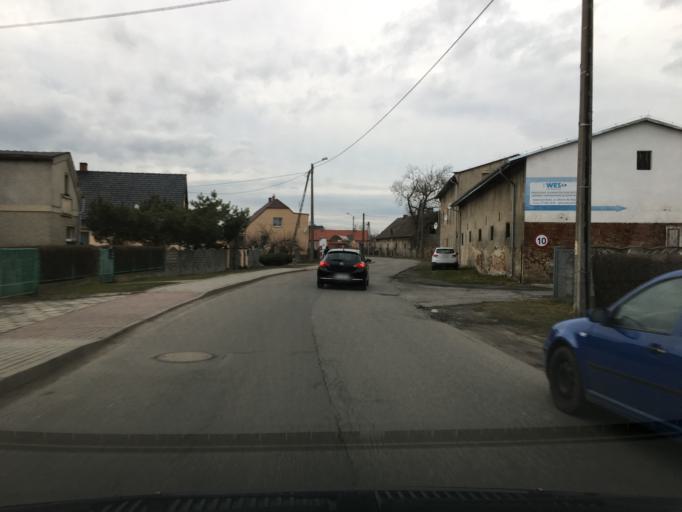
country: PL
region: Opole Voivodeship
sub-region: Powiat kedzierzynsko-kozielski
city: Kozle
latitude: 50.3546
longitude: 18.1311
